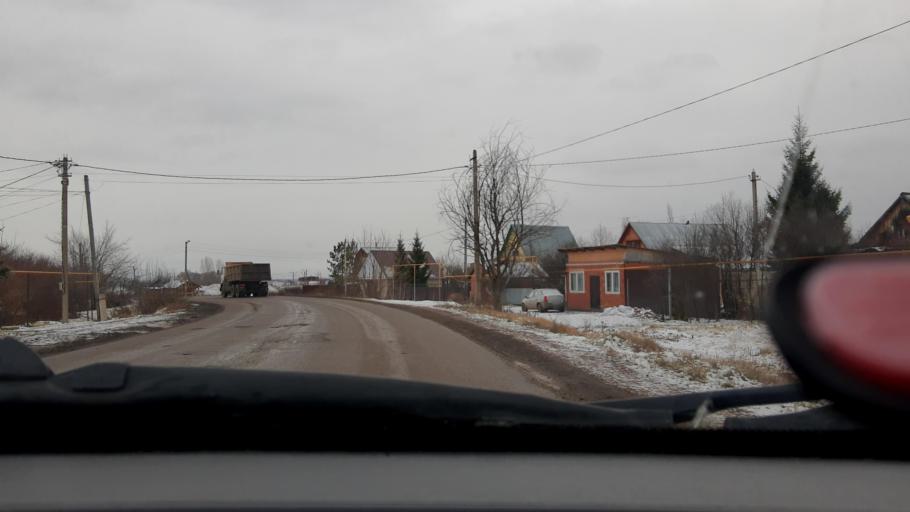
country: RU
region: Bashkortostan
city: Ufa
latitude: 54.5634
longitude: 55.9383
